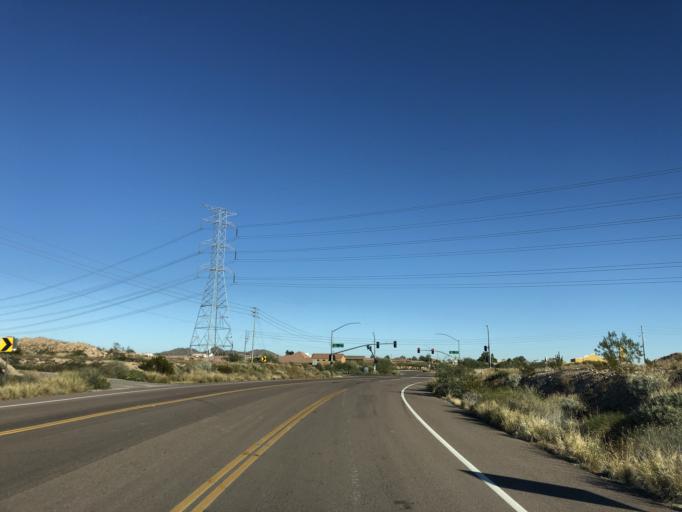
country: US
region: Arizona
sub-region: Maricopa County
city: Sun City West
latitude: 33.6960
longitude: -112.2912
